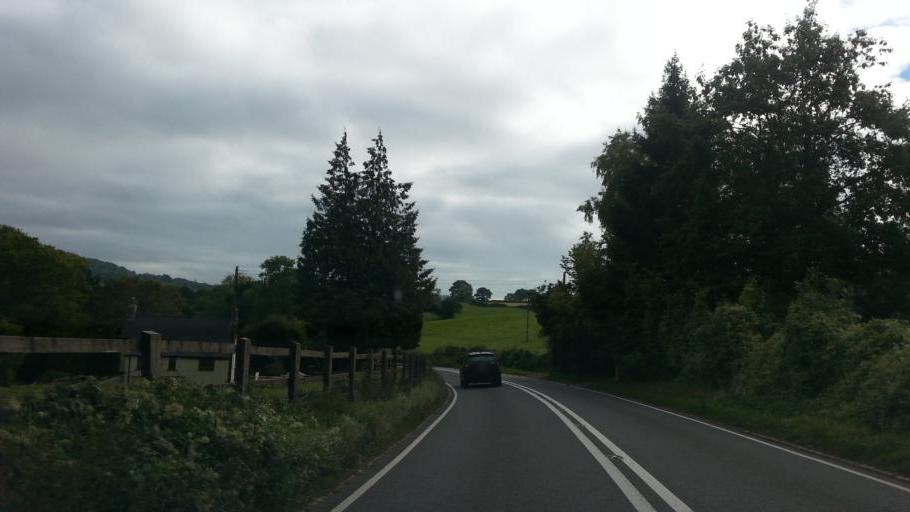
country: GB
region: England
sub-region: Gloucestershire
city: Mitcheldean
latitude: 51.8847
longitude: -2.4785
